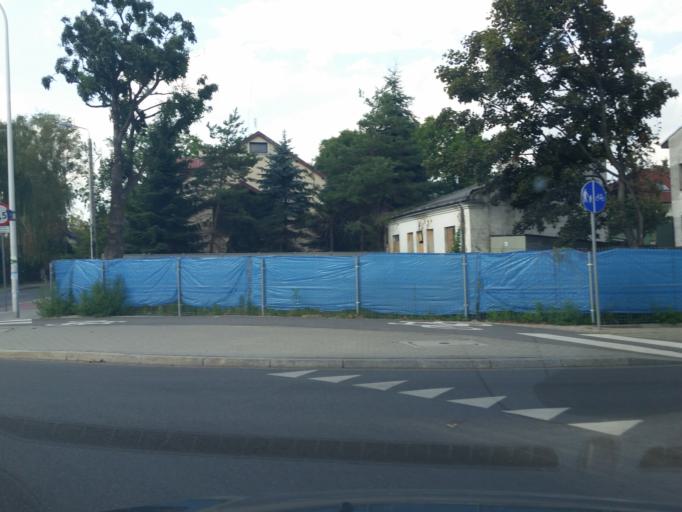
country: PL
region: Masovian Voivodeship
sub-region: Warszawa
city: Ursus
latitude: 52.1999
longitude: 20.9144
